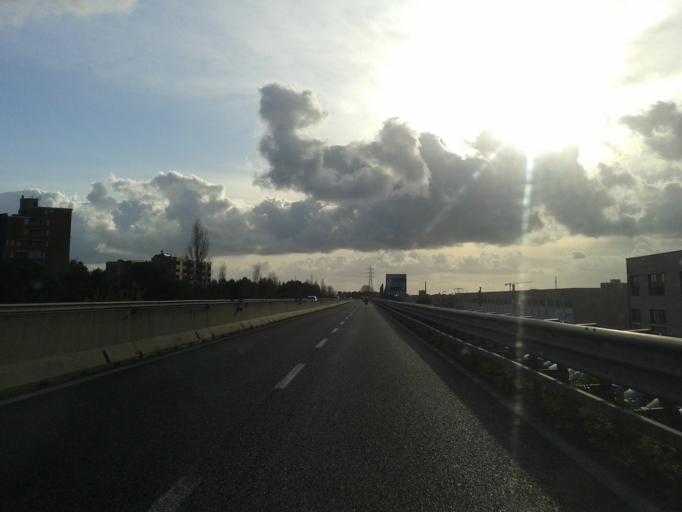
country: IT
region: Tuscany
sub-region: Provincia di Livorno
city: Livorno
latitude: 43.5401
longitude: 10.3373
